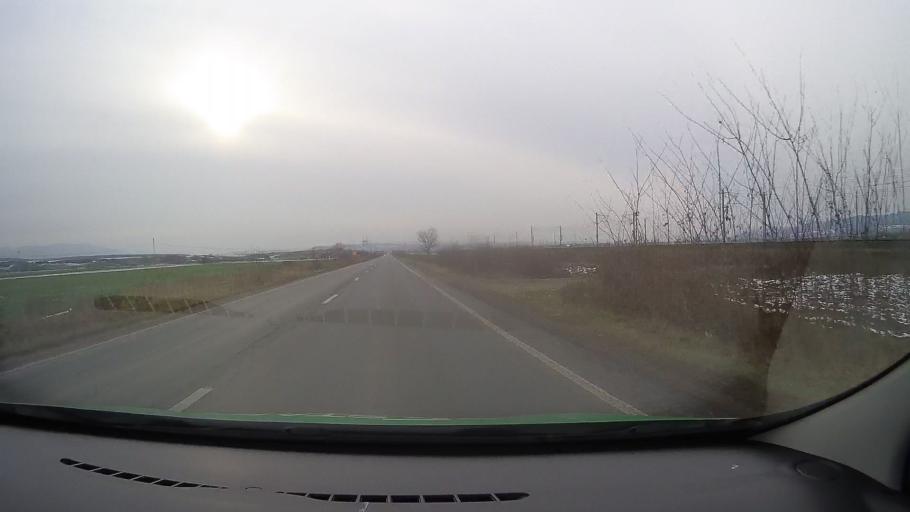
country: RO
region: Hunedoara
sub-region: Comuna Geoagiu
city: Geoagiu
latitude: 45.8796
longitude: 23.2429
